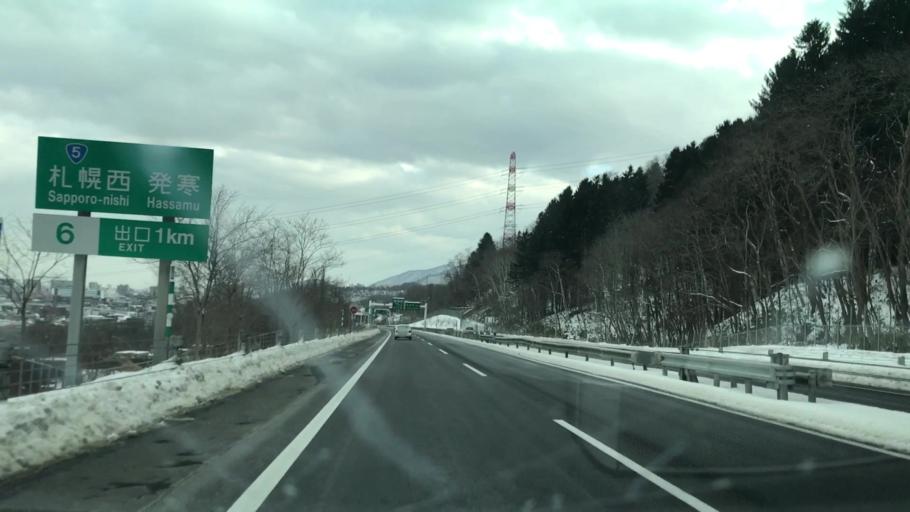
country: JP
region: Hokkaido
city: Sapporo
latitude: 43.0979
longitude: 141.2506
